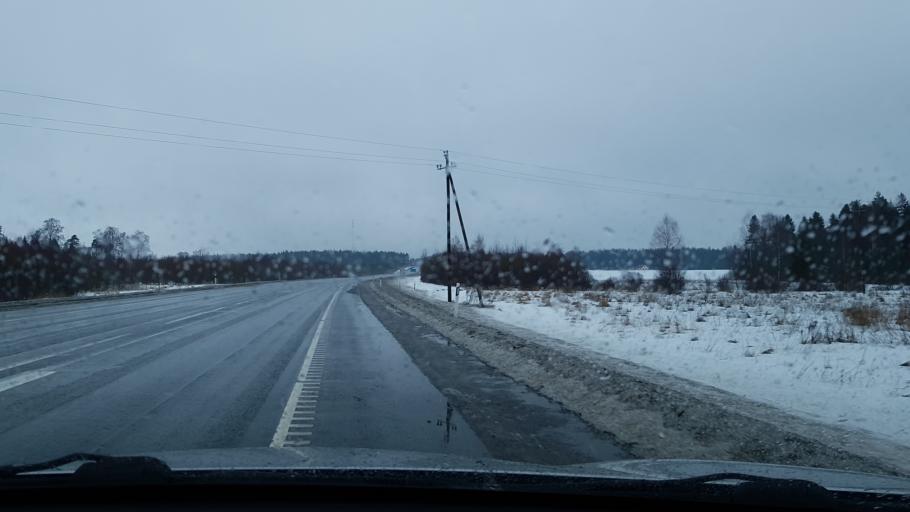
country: EE
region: Raplamaa
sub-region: Kohila vald
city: Kohila
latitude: 59.1744
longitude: 24.7746
